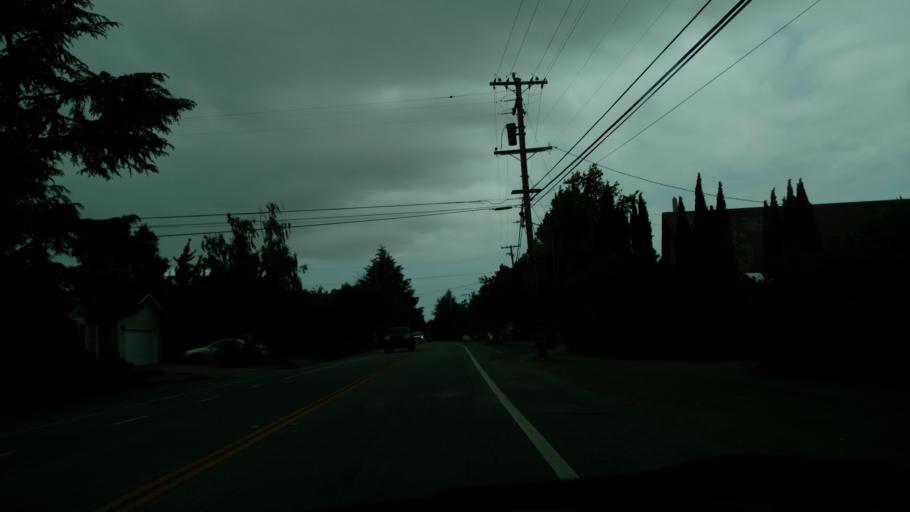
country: US
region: California
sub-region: Santa Clara County
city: Mountain View
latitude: 37.3793
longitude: -122.0960
